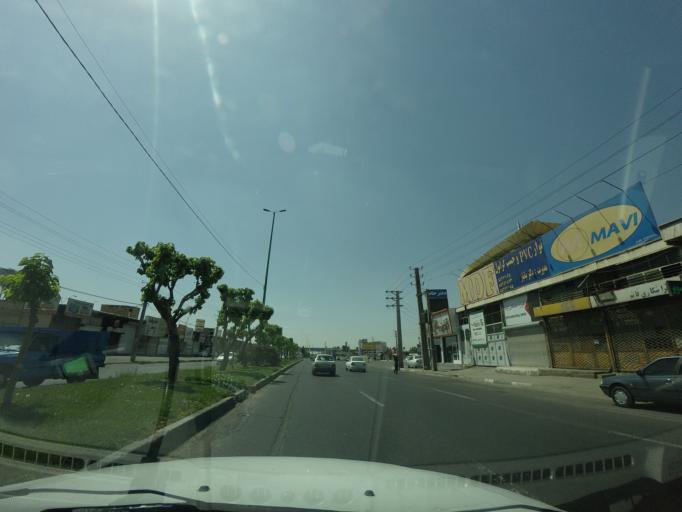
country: IR
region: Tehran
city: Eslamshahr
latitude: 35.6024
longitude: 51.3017
